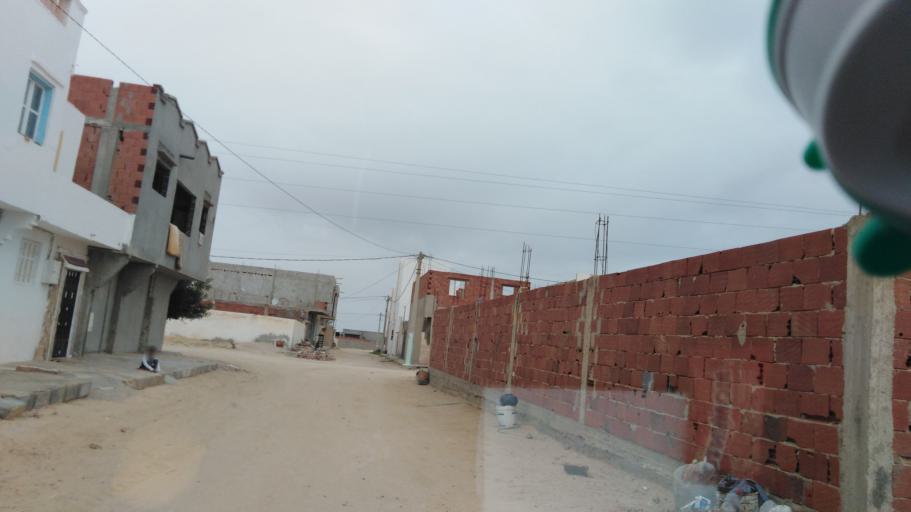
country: TN
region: Qabis
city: Gabes
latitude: 33.9515
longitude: 10.0037
